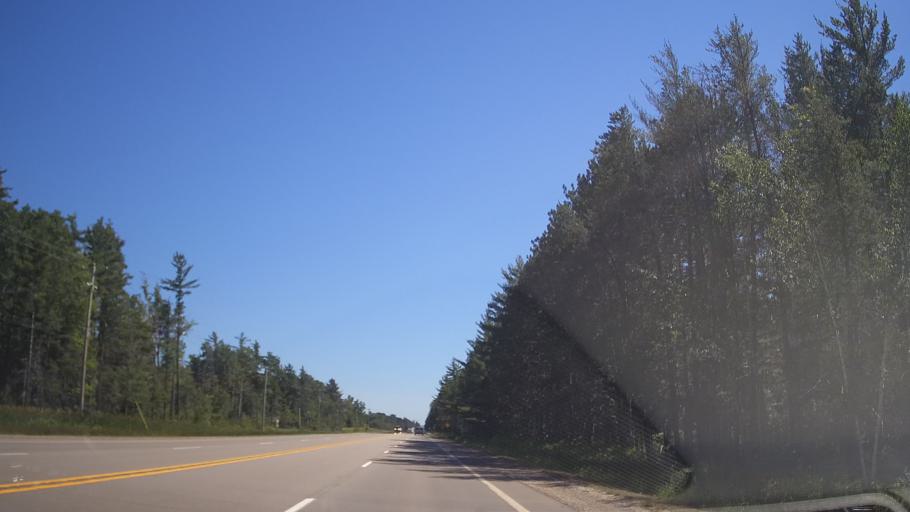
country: US
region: Michigan
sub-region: Cheboygan County
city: Indian River
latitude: 45.5197
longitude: -84.7816
